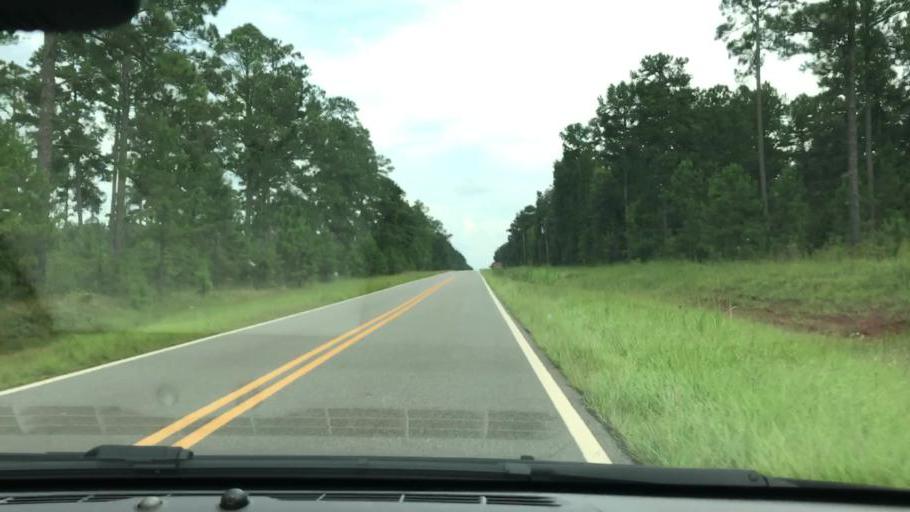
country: US
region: Georgia
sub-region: Early County
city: Blakely
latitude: 31.4598
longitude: -84.9192
